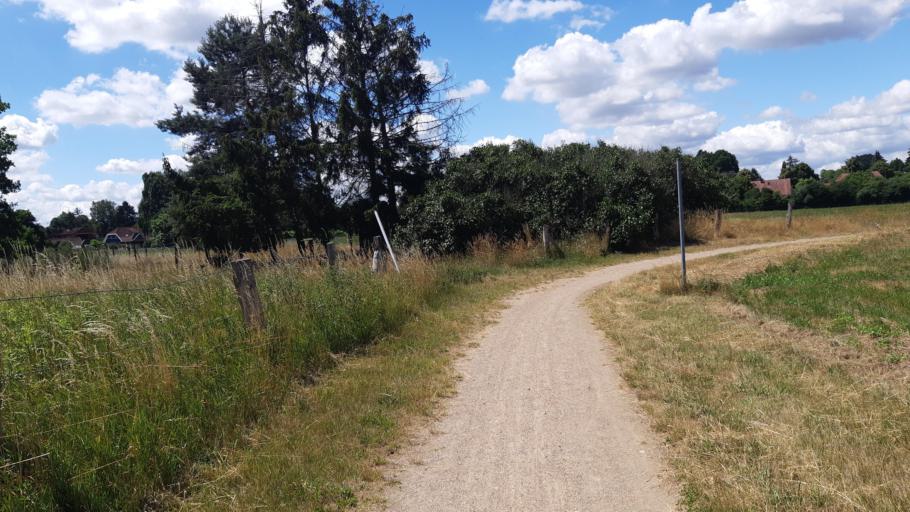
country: DE
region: Lower Saxony
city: Dahlenburg
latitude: 53.1906
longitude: 10.7403
